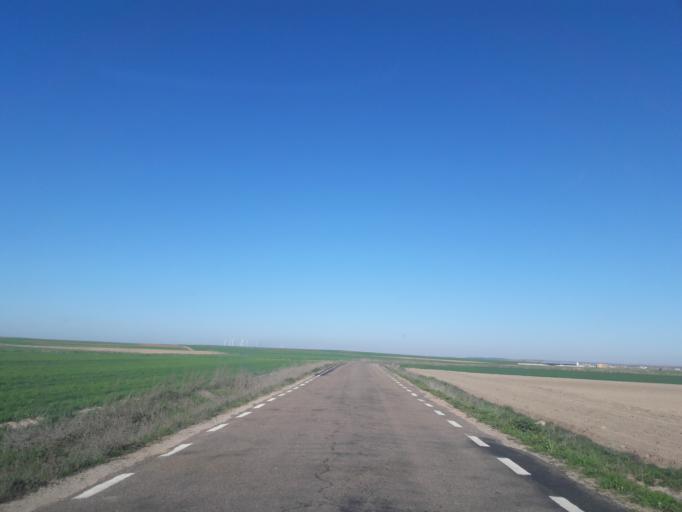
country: ES
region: Castille and Leon
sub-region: Provincia de Salamanca
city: Tordillos
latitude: 40.8613
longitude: -5.3655
